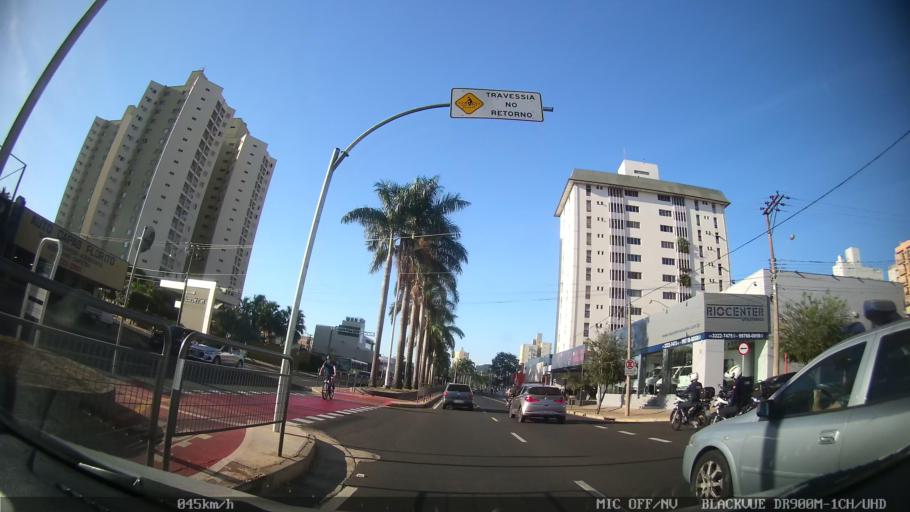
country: BR
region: Sao Paulo
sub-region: Sao Jose Do Rio Preto
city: Sao Jose do Rio Preto
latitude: -20.8161
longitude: -49.3931
